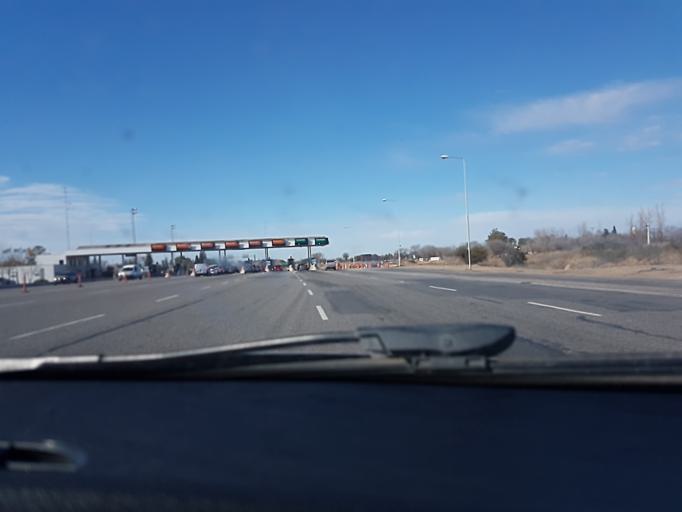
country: AR
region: Cordoba
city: Villa Allende
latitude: -31.3118
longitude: -64.2194
